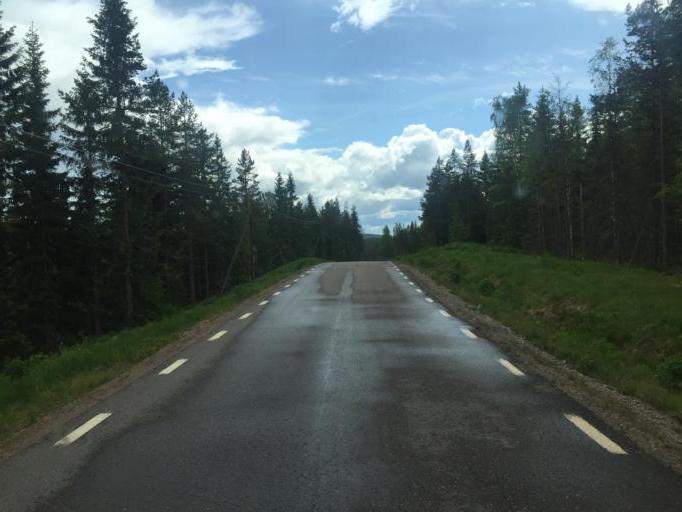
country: SE
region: Vaermland
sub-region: Hagfors Kommun
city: Hagfors
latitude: 60.2986
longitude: 13.8677
